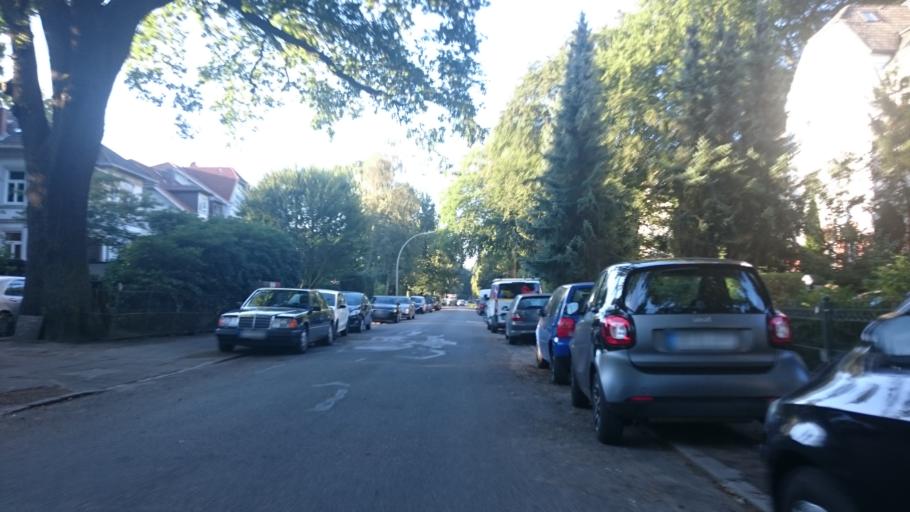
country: DE
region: Hamburg
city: Eidelstedt
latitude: 53.5718
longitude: 9.8985
